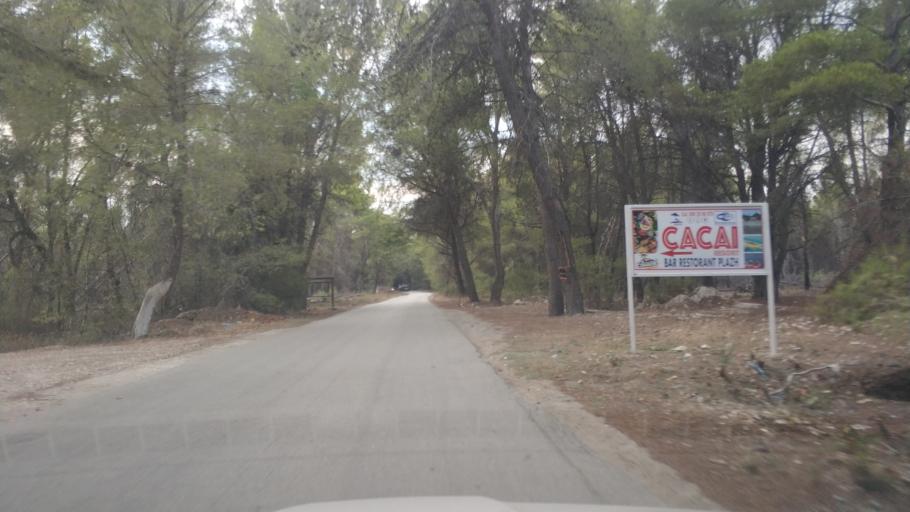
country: AL
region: Vlore
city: Vlore
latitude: 40.4847
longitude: 19.4462
